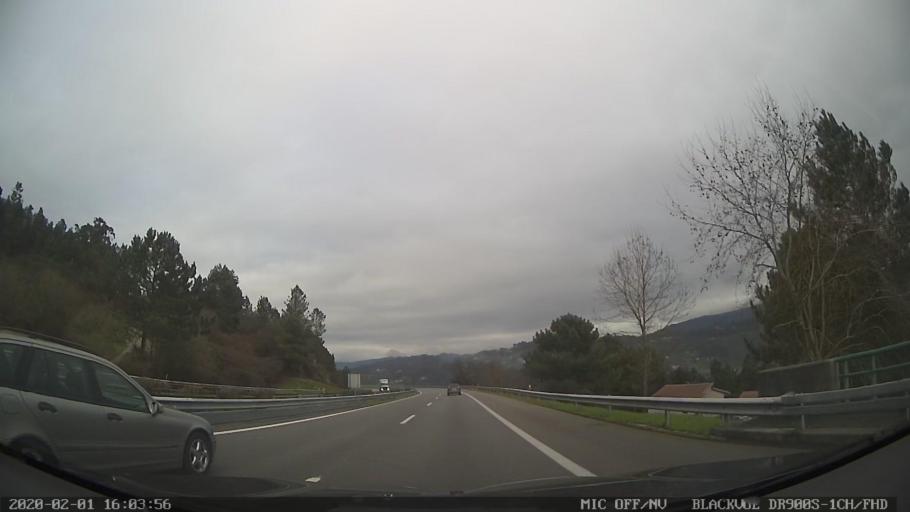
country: PT
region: Porto
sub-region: Marco de Canaveses
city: Marco de Canavezes
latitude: 41.2335
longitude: -8.1264
